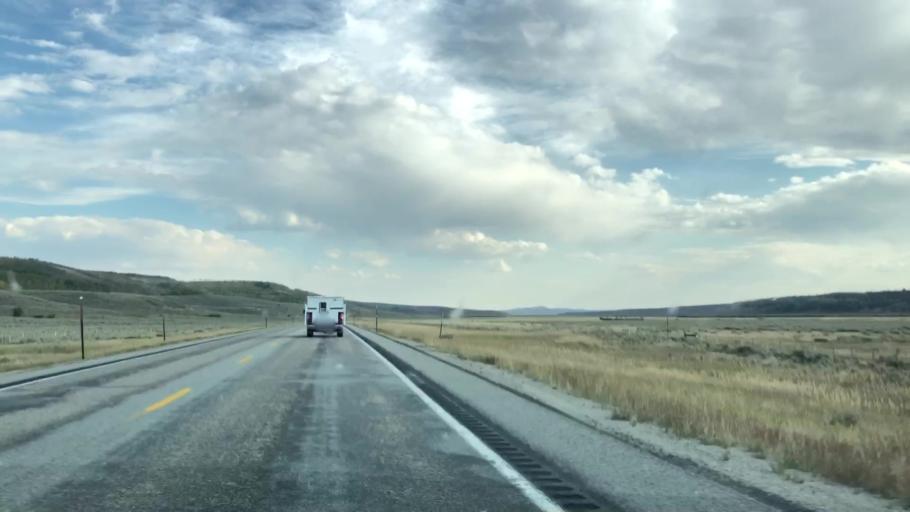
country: US
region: Wyoming
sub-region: Sublette County
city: Pinedale
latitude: 43.1035
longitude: -110.1705
